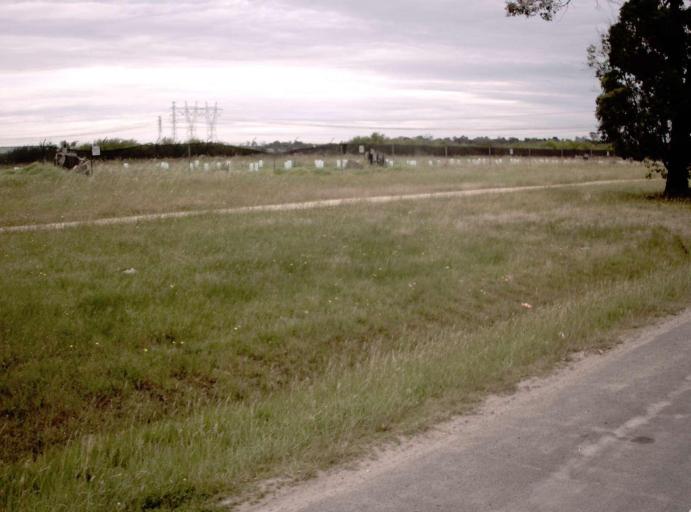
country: AU
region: Victoria
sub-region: Casey
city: Lynbrook
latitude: -38.0601
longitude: 145.2636
